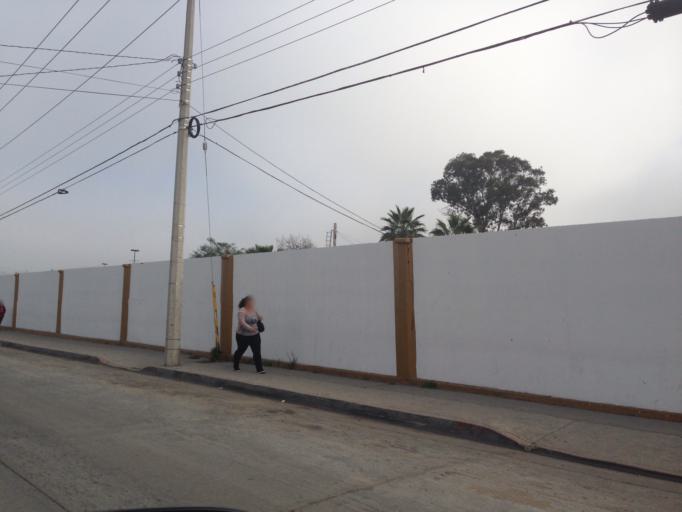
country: MX
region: Baja California
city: Tijuana
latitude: 32.5058
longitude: -116.9989
